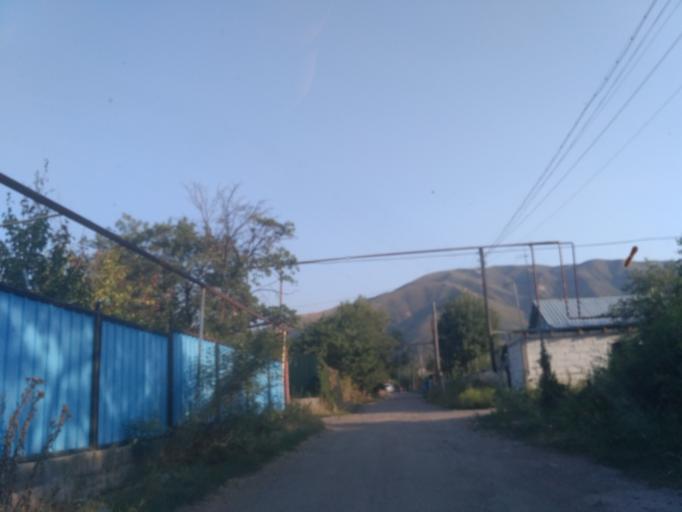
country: KZ
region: Almaty Oblysy
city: Burunday
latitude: 43.1648
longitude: 76.4046
